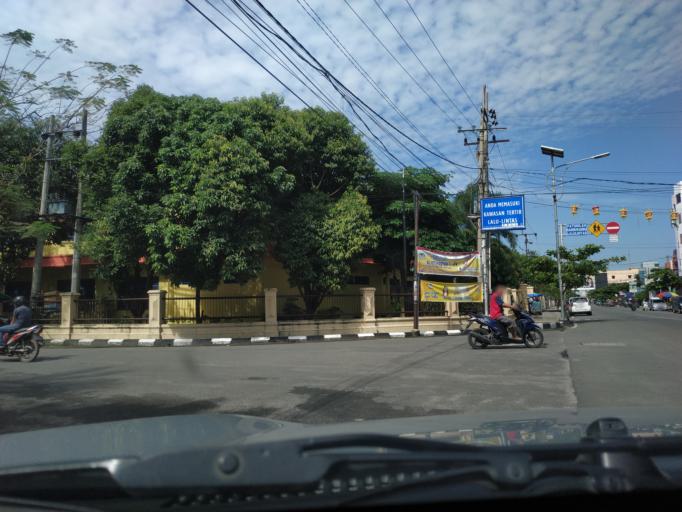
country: ID
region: North Sumatra
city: Tebingtinggi
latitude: 3.3271
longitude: 99.1655
